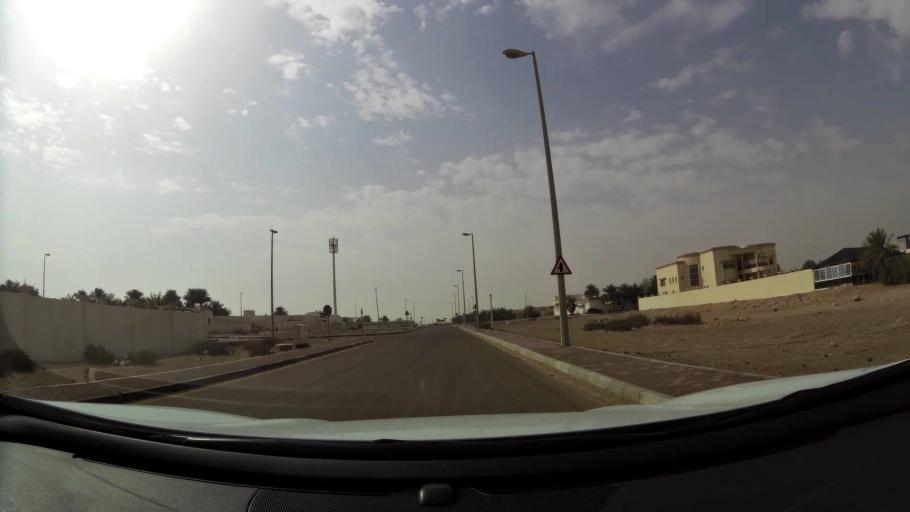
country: AE
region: Abu Dhabi
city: Abu Dhabi
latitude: 24.2749
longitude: 54.6716
